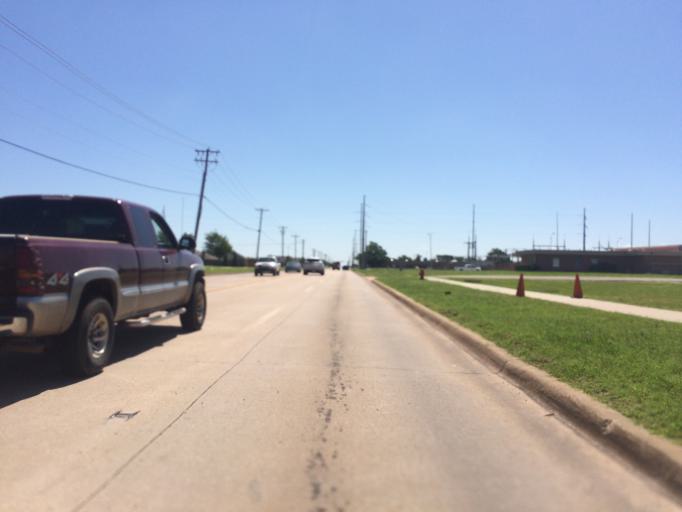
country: US
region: Oklahoma
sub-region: Cleveland County
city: Norman
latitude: 35.2474
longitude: -97.4570
